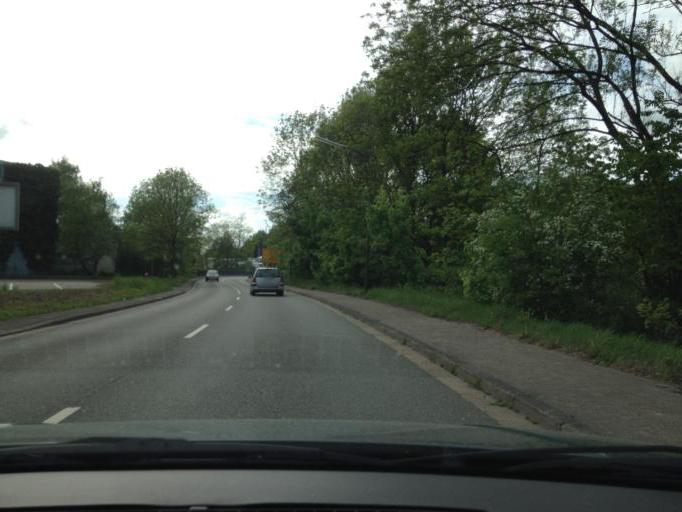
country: DE
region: Saarland
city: Hangard
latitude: 49.3546
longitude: 7.2198
